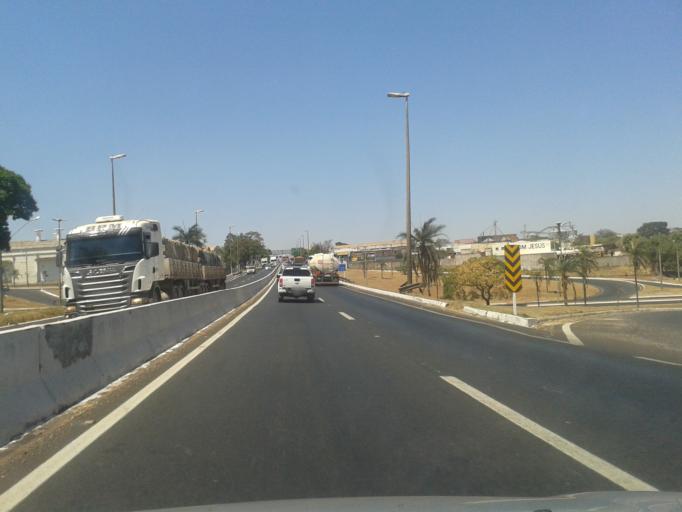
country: BR
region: Minas Gerais
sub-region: Uberlandia
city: Uberlandia
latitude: -18.8930
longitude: -48.2523
